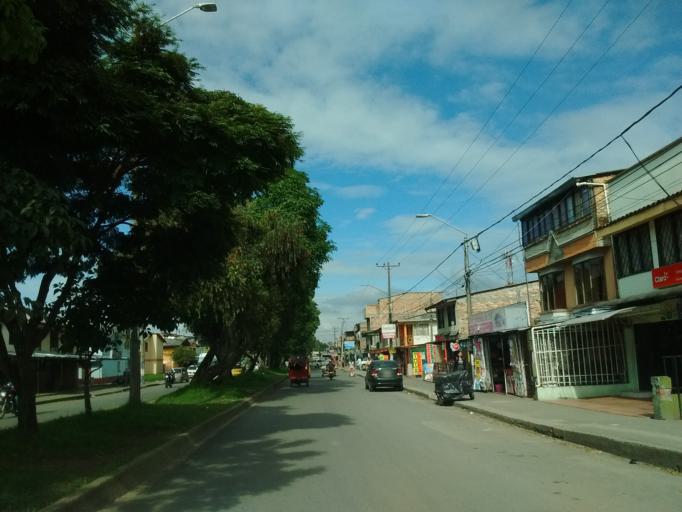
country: CO
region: Cauca
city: Popayan
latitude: 2.4361
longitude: -76.6134
